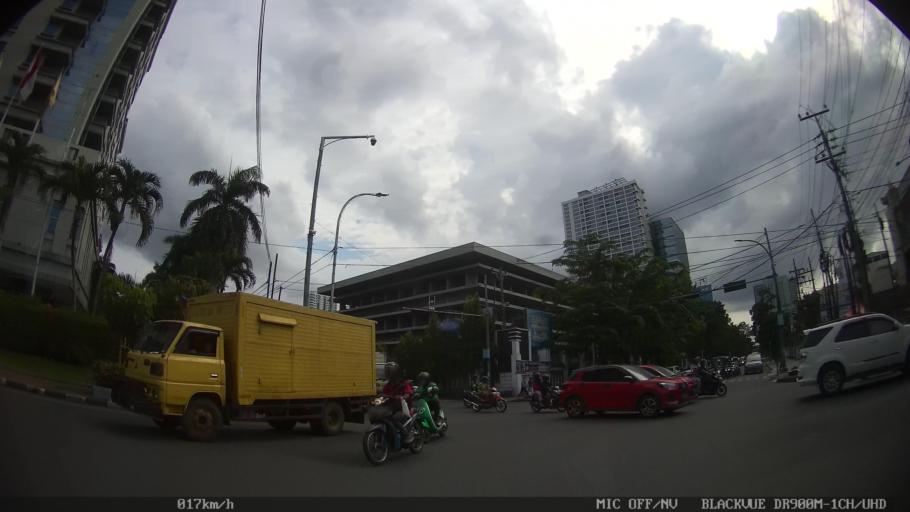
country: ID
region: North Sumatra
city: Medan
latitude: 3.5988
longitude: 98.6808
